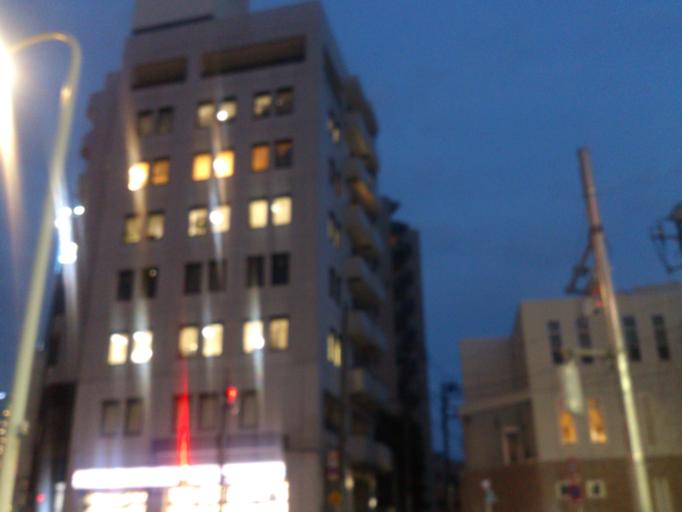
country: JP
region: Tokyo
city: Tokyo
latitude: 35.6589
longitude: 139.7153
